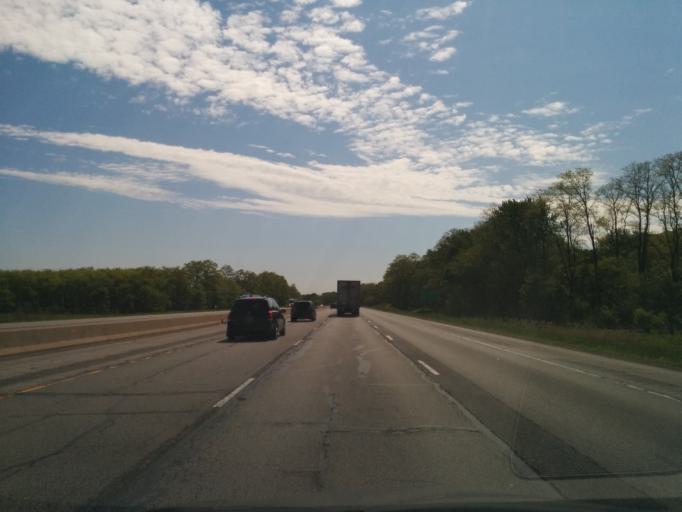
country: US
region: Indiana
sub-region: Porter County
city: Portage
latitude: 41.6017
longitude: -87.1576
